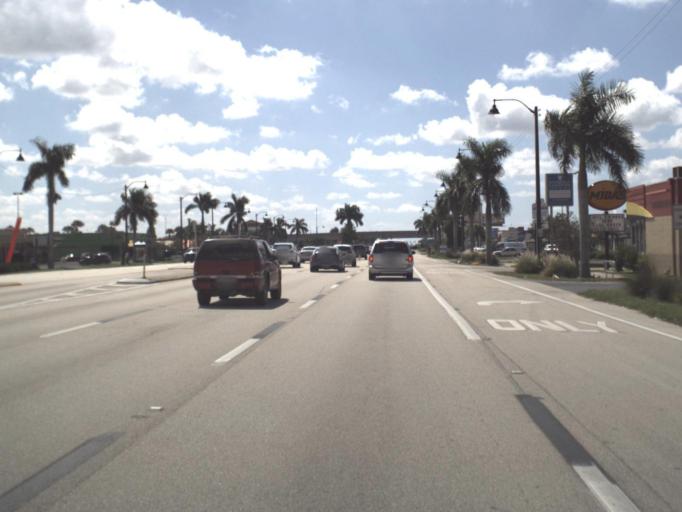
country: US
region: Florida
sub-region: Lee County
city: Pine Manor
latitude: 26.6010
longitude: -81.8719
